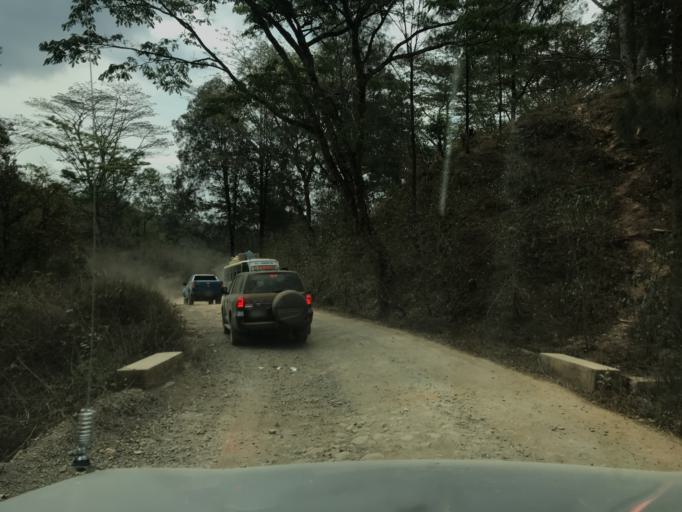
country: TL
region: Ermera
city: Gleno
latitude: -8.8253
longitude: 125.4357
